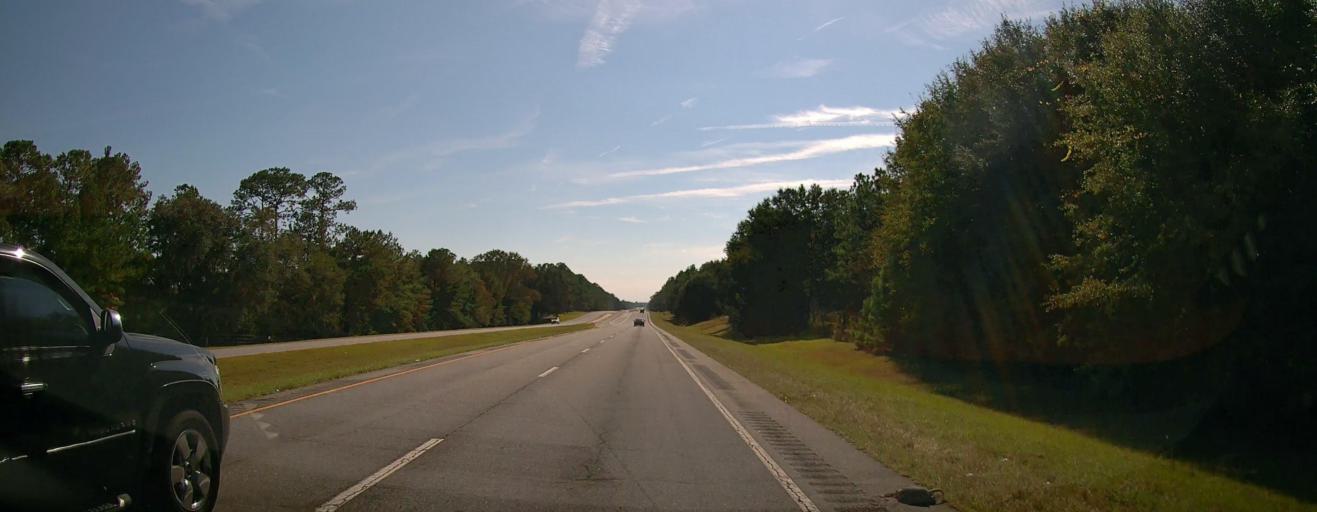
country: US
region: Georgia
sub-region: Lee County
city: Leesburg
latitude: 31.6875
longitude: -83.9936
